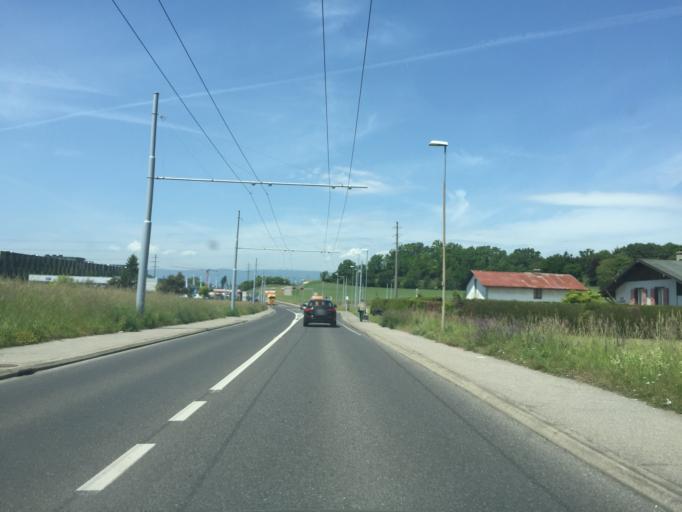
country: CH
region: Vaud
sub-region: Ouest Lausannois District
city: Renens
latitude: 46.5266
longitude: 6.5848
